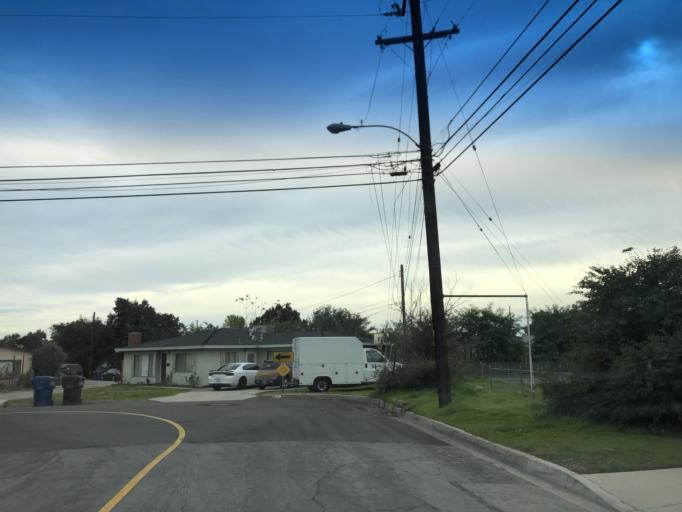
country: US
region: California
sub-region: Los Angeles County
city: Arcadia
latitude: 34.1382
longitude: -118.0174
